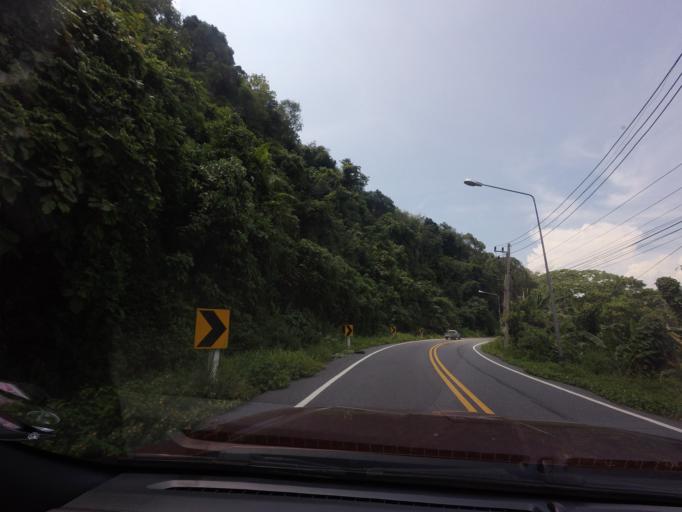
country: TH
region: Yala
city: Than To
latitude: 6.0357
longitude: 101.2079
